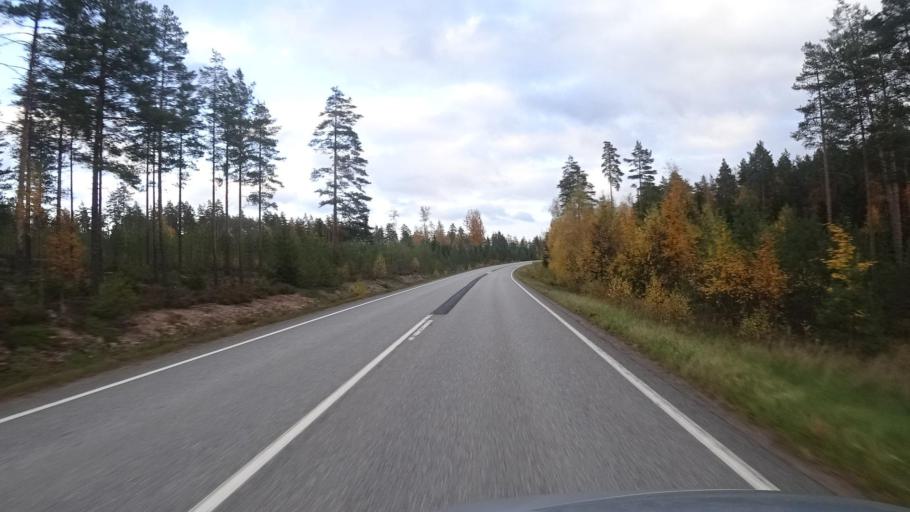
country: FI
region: Satakunta
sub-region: Pori
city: Vampula
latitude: 60.9835
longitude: 22.5502
